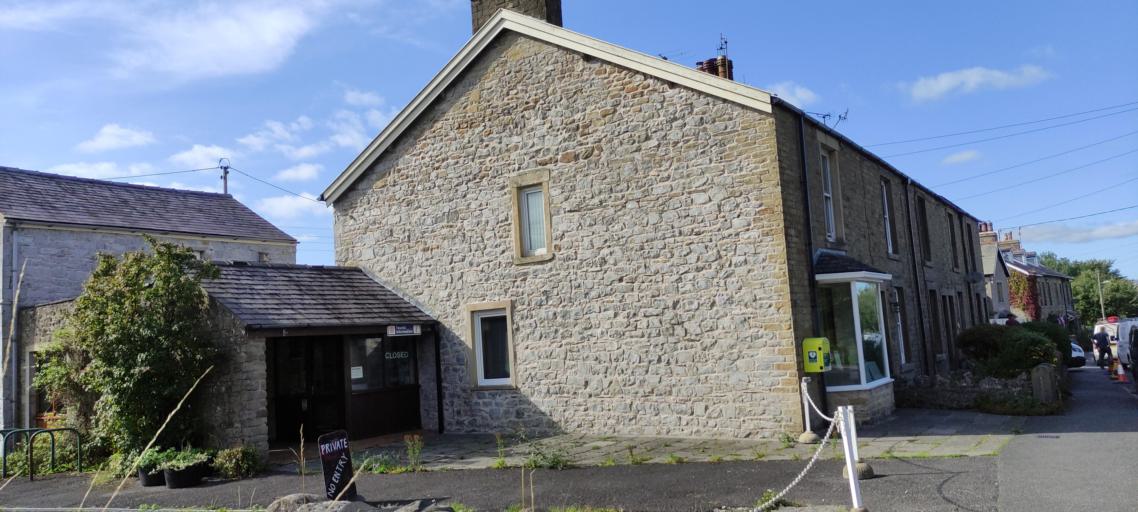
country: GB
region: England
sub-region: North Yorkshire
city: Settle
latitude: 54.1478
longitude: -2.2948
